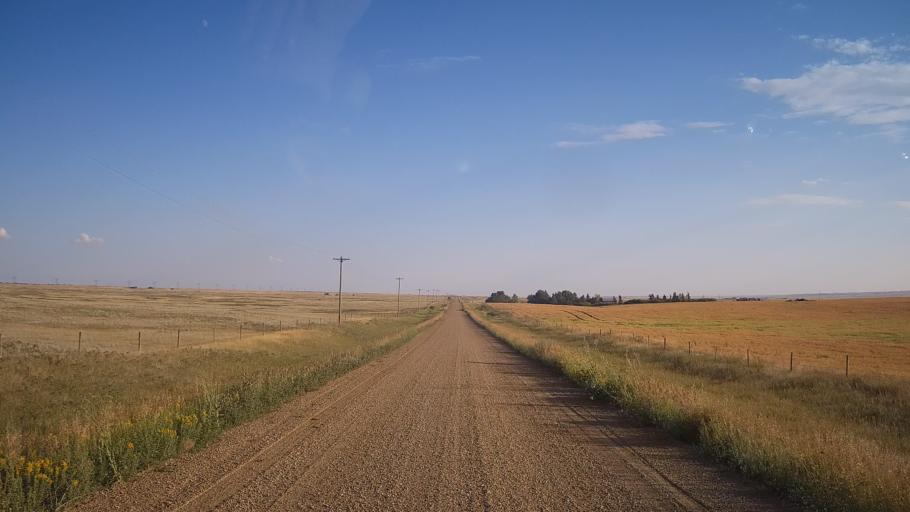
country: CA
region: Alberta
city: Hanna
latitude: 51.6190
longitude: -111.8569
